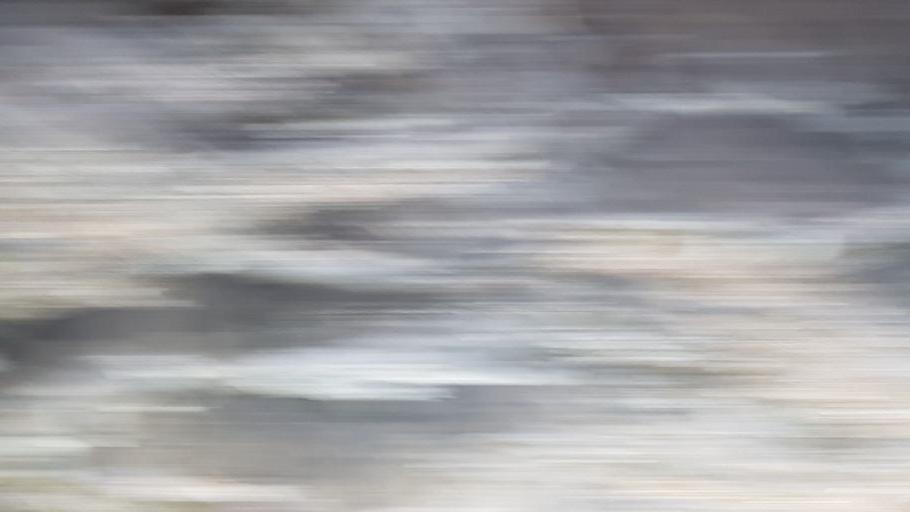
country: NO
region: Nord-Trondelag
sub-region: Levanger
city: Skogn
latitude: 63.6732
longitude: 11.1124
